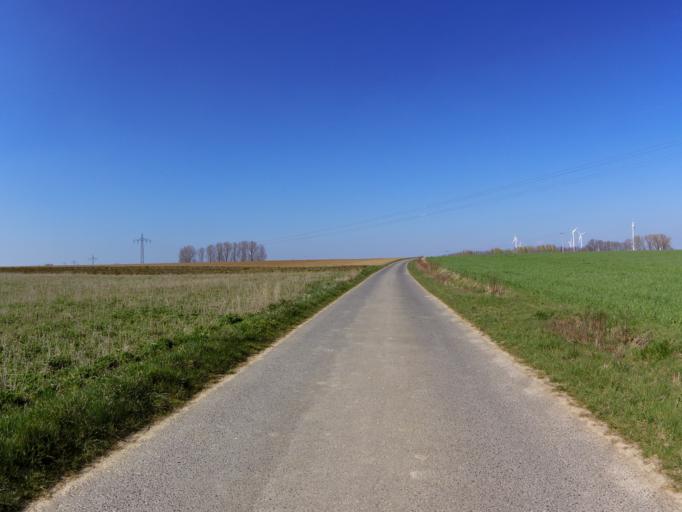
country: DE
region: Bavaria
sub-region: Regierungsbezirk Unterfranken
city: Biebelried
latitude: 49.7369
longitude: 10.0873
